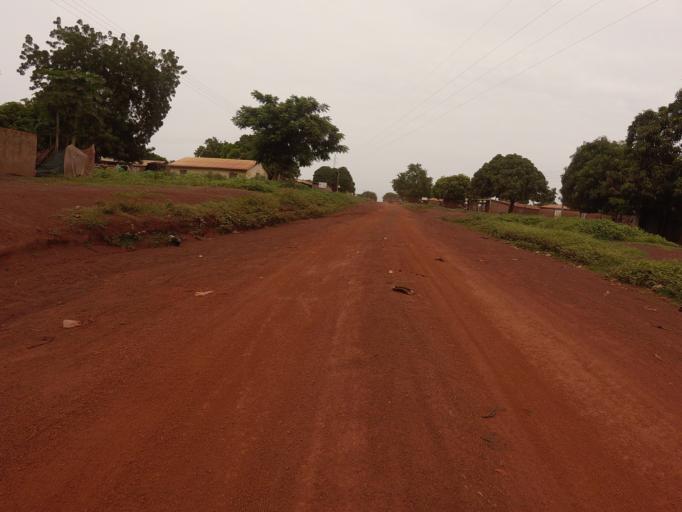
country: GH
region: Northern
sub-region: Yendi
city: Yendi
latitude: 9.0386
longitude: -0.0129
